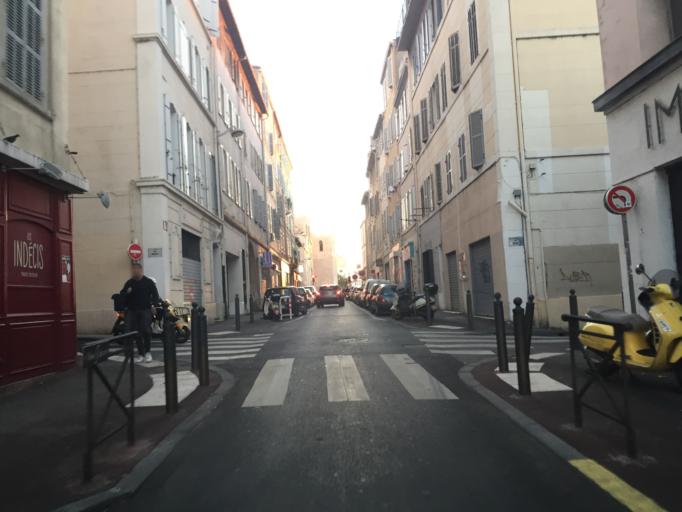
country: FR
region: Provence-Alpes-Cote d'Azur
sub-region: Departement des Bouches-du-Rhone
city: Marseille 02
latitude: 43.2909
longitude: 5.3676
